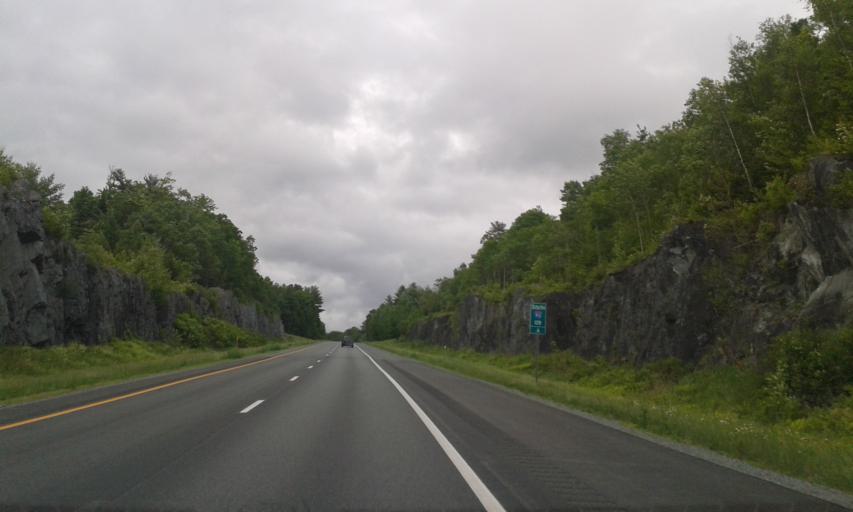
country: US
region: New Hampshire
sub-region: Grafton County
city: Littleton
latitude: 44.3128
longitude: -71.8510
